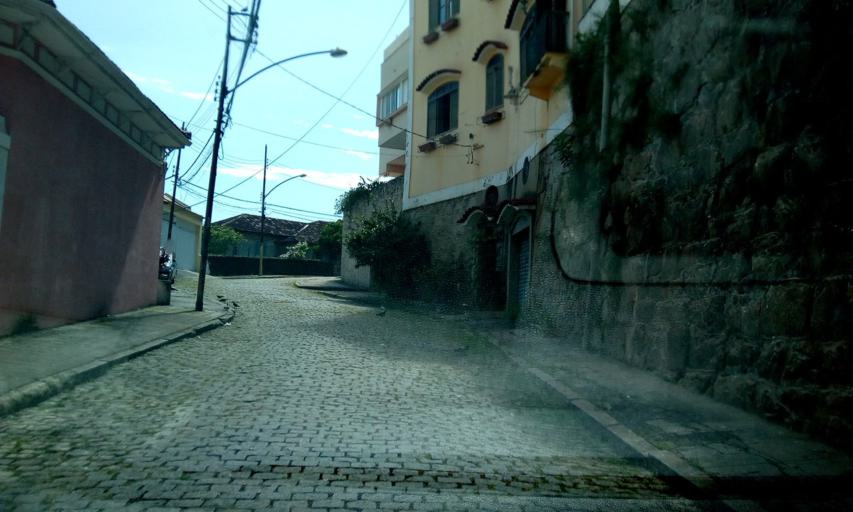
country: BR
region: Rio de Janeiro
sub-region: Rio De Janeiro
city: Rio de Janeiro
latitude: -22.9233
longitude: -43.1902
